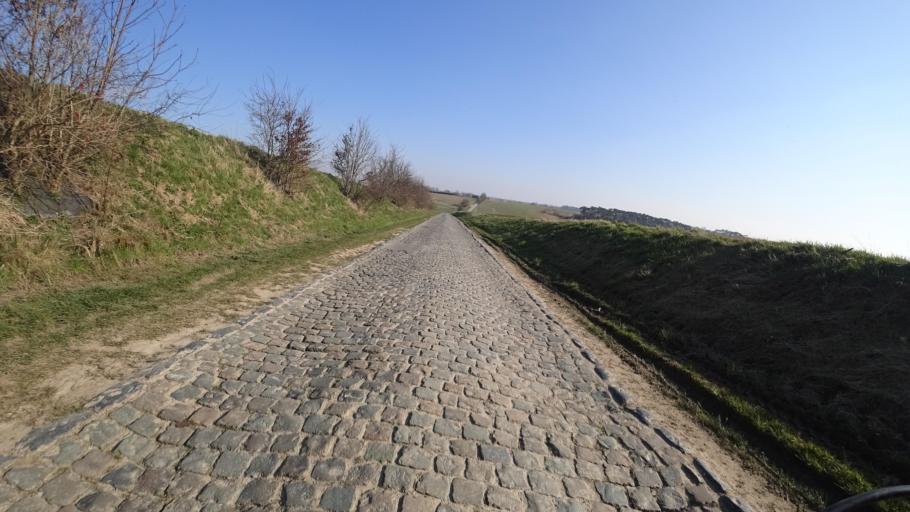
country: BE
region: Wallonia
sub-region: Province du Brabant Wallon
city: Mont-Saint-Guibert
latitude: 50.6077
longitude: 4.5919
